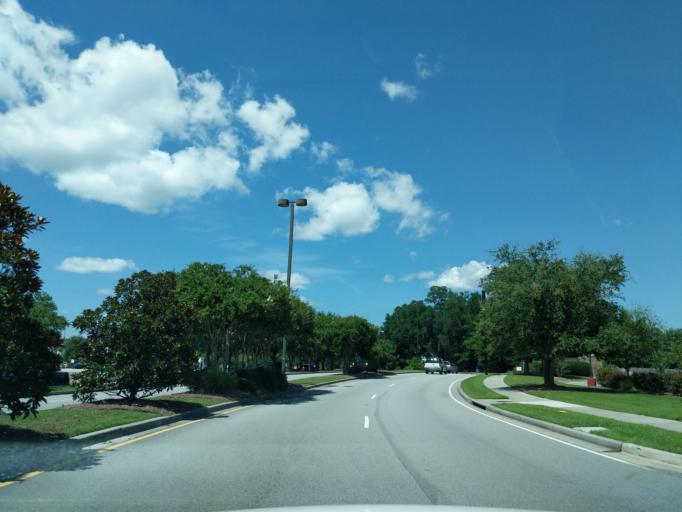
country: US
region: South Carolina
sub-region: Charleston County
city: North Charleston
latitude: 32.8726
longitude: -80.0161
